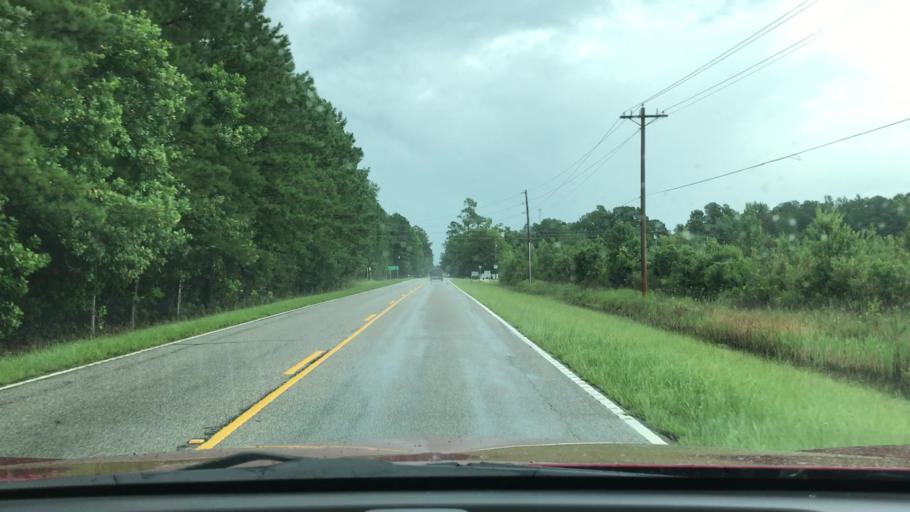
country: US
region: South Carolina
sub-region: Georgetown County
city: Georgetown
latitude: 33.5285
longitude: -79.2400
